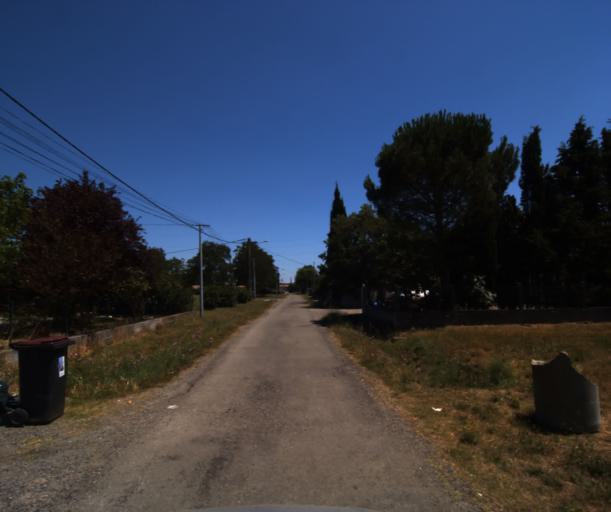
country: FR
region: Midi-Pyrenees
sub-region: Departement de la Haute-Garonne
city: Seysses
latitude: 43.4644
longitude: 1.3096
